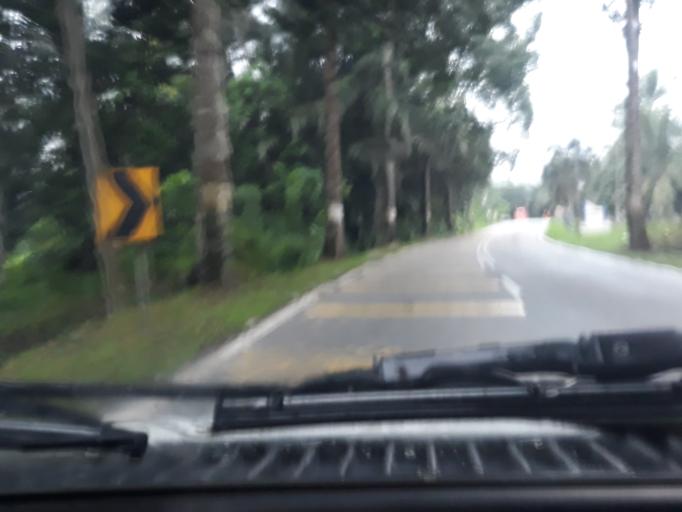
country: MY
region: Kedah
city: Kulim
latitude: 5.2480
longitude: 100.6027
